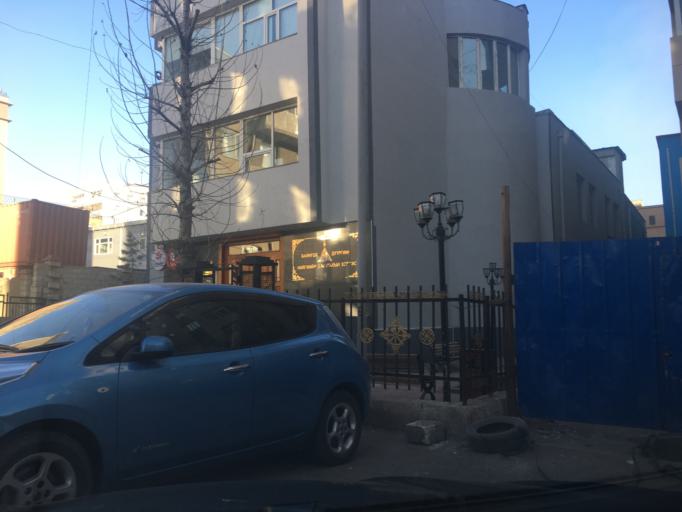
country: MN
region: Ulaanbaatar
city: Ulaanbaatar
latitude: 47.9178
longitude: 106.8891
